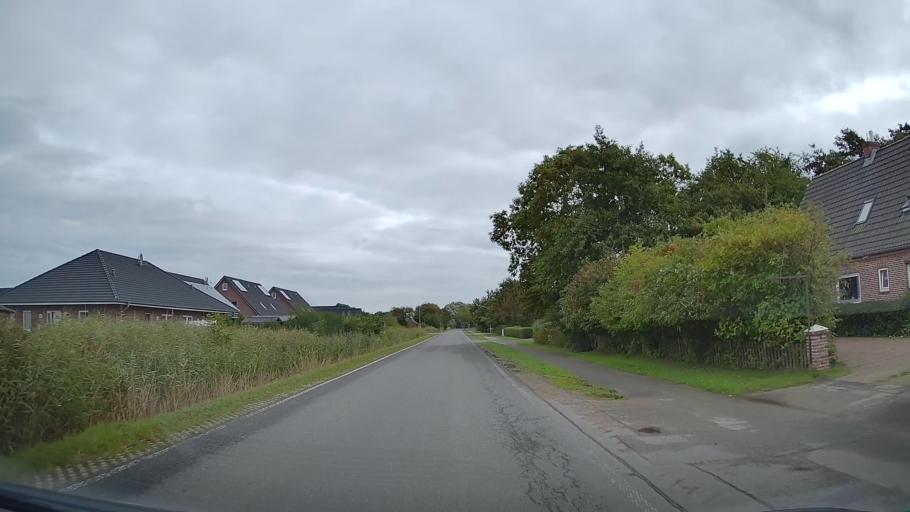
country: DE
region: Schleswig-Holstein
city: Klanxbull
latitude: 54.8669
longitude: 8.6707
